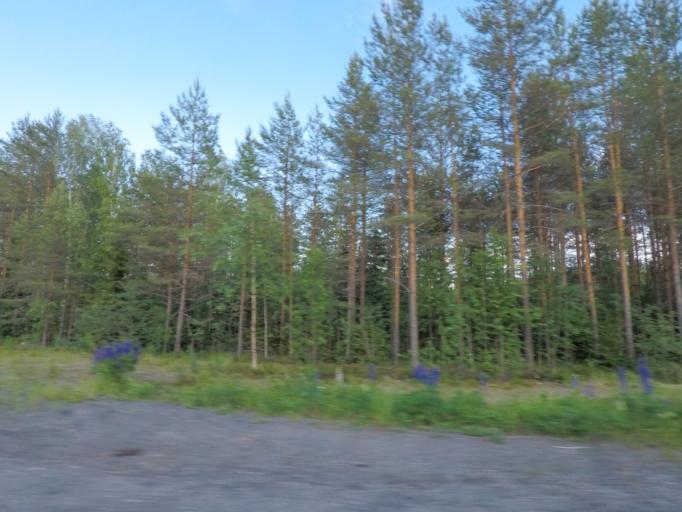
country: FI
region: Central Finland
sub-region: Jyvaeskylae
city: Toivakka
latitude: 62.0784
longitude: 26.0460
